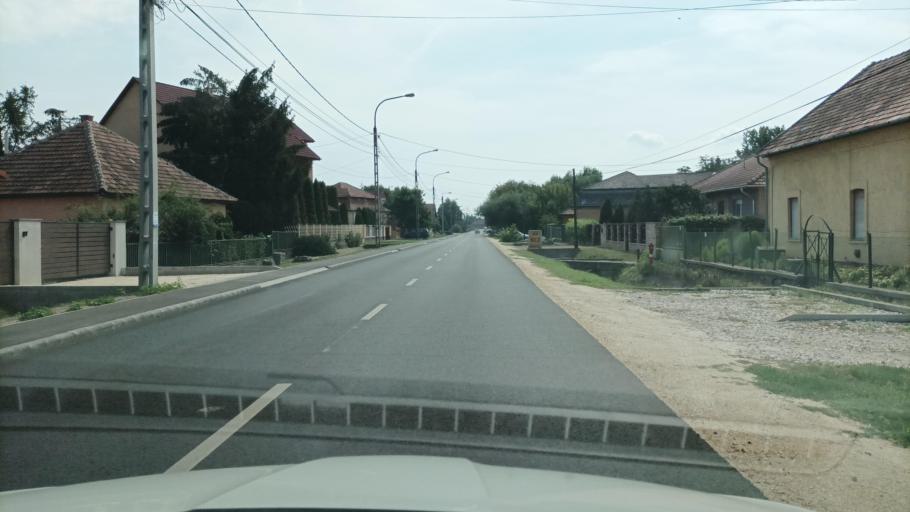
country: HU
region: Pest
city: Tura
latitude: 47.6202
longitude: 19.5976
